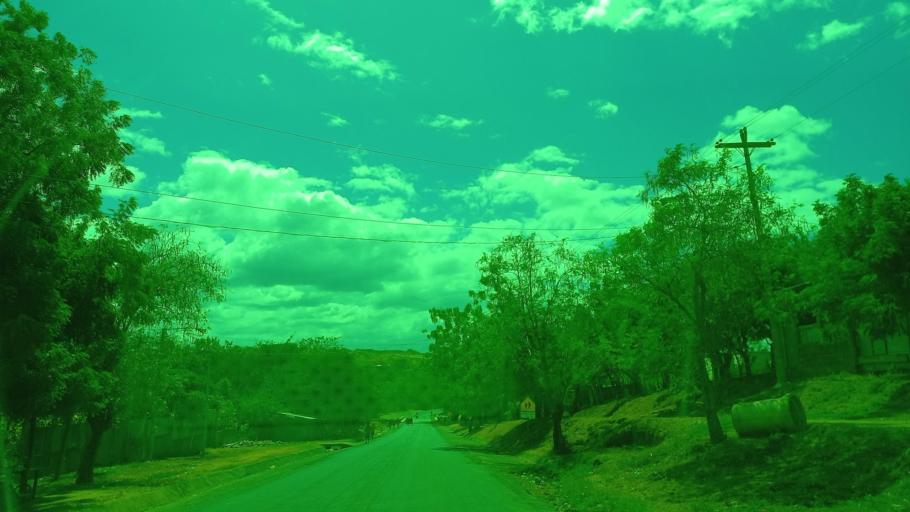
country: NI
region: Managua
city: Ciudad Sandino
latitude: 12.1891
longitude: -86.3367
